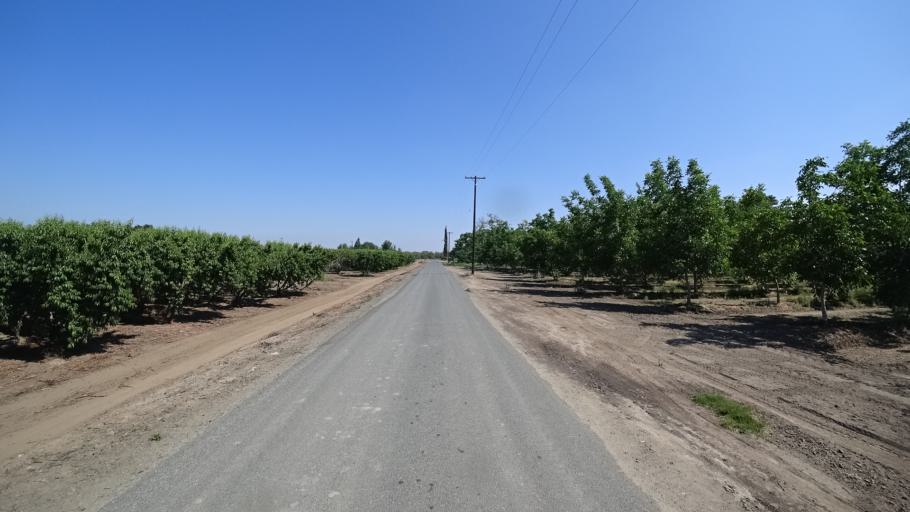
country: US
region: California
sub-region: Fresno County
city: Kingsburg
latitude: 36.4471
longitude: -119.5630
